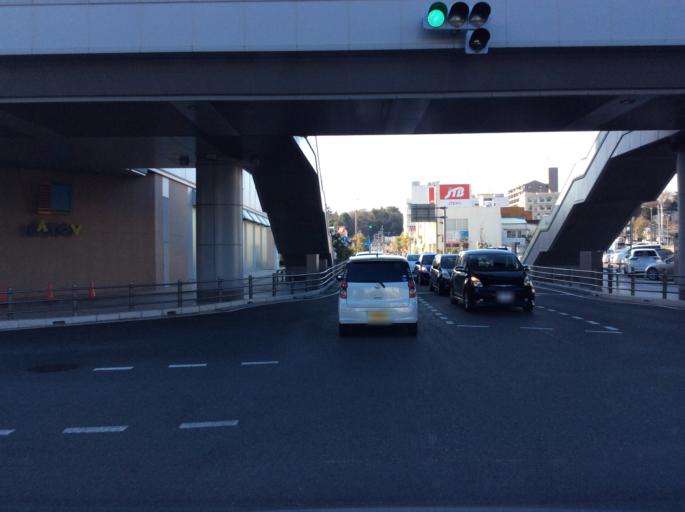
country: JP
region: Fukushima
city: Iwaki
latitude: 37.0575
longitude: 140.8923
